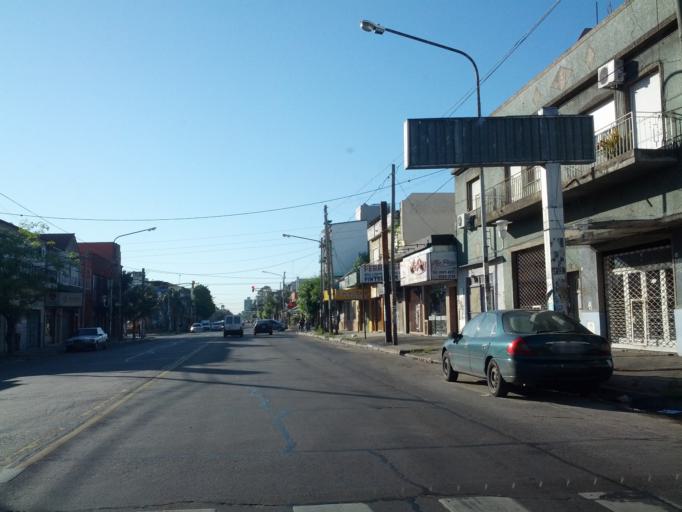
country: AR
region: Buenos Aires
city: San Justo
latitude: -34.6632
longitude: -58.5402
